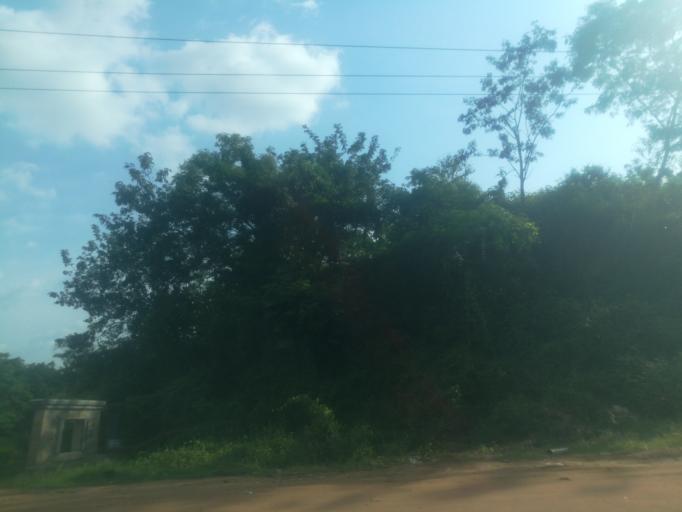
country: NG
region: Oyo
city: Ido
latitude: 7.3958
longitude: 3.7816
